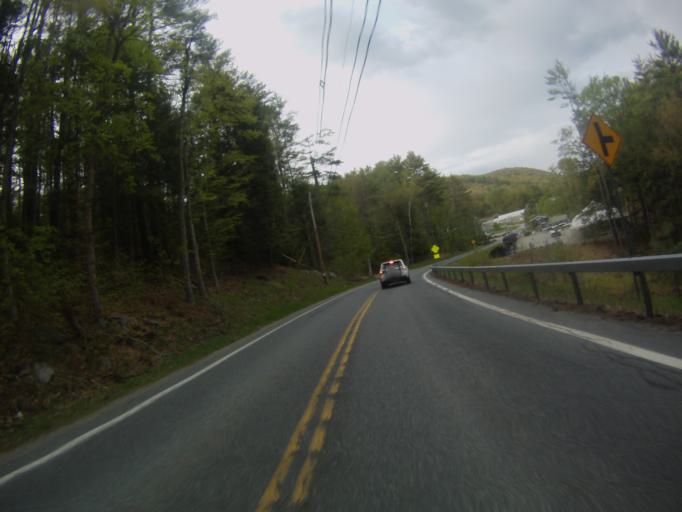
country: US
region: New York
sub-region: Warren County
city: Warrensburg
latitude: 43.6721
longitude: -73.7598
